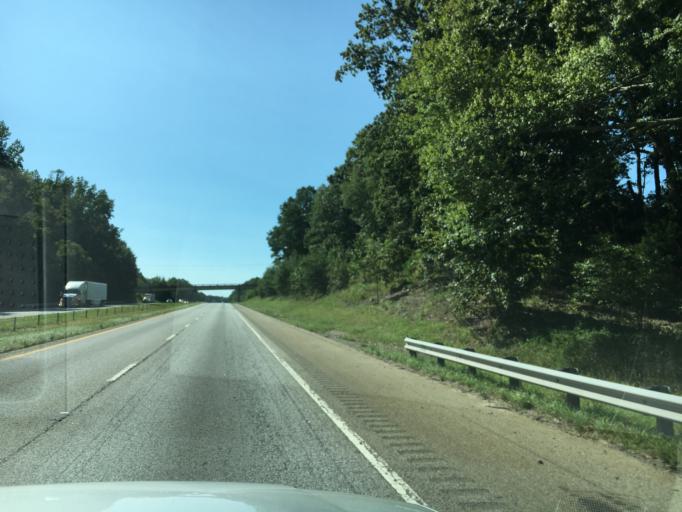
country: US
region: South Carolina
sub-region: Spartanburg County
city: Roebuck
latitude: 34.7894
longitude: -81.9560
